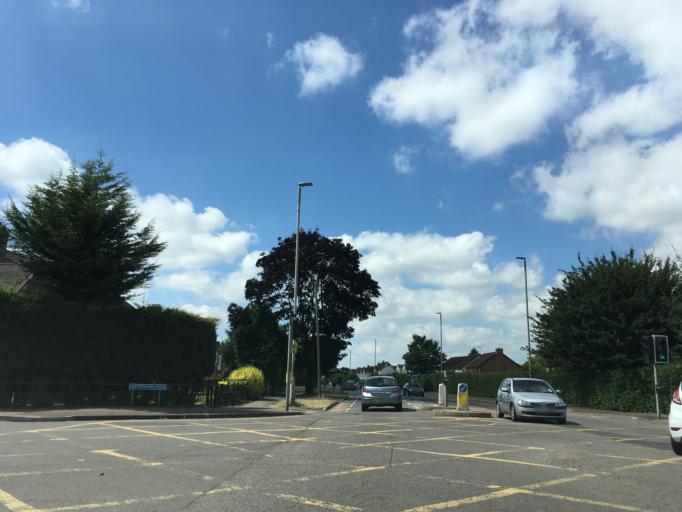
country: GB
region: England
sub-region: Gloucestershire
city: Barnwood
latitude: 51.8772
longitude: -2.2034
